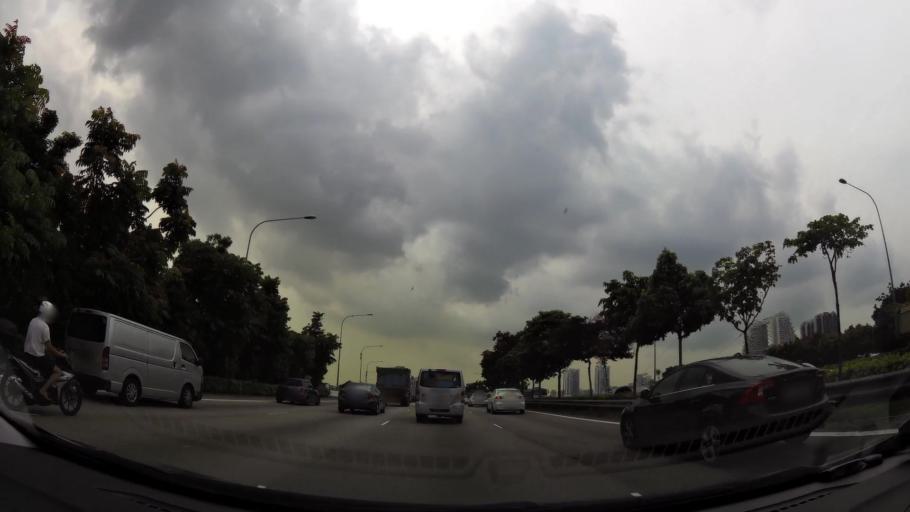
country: SG
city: Singapore
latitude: 1.3563
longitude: 103.8570
